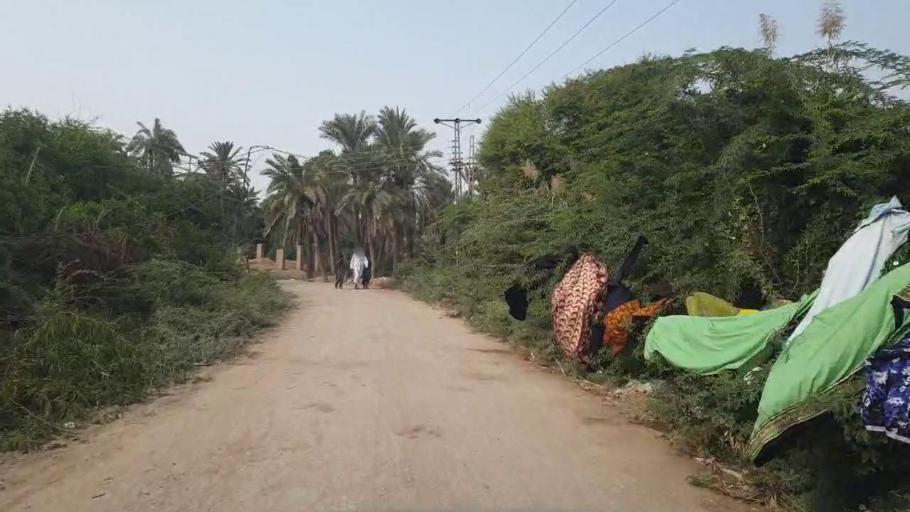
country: PK
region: Sindh
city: Tando Muhammad Khan
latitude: 25.1151
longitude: 68.3673
